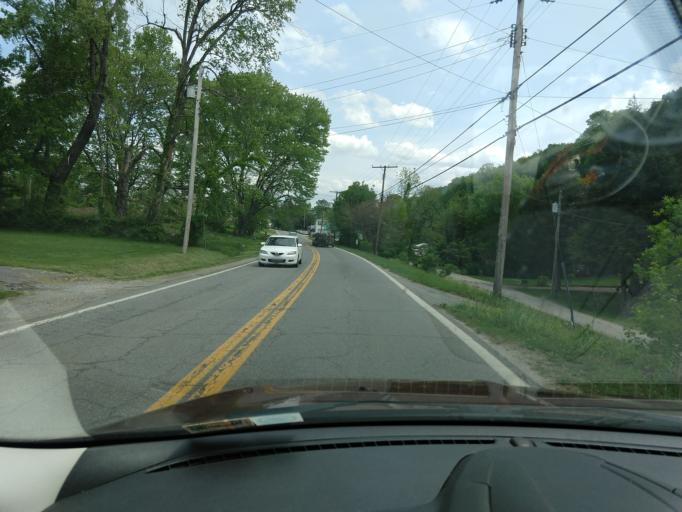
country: US
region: West Virginia
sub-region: Kanawha County
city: Cross Lanes
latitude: 38.3746
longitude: -81.7860
